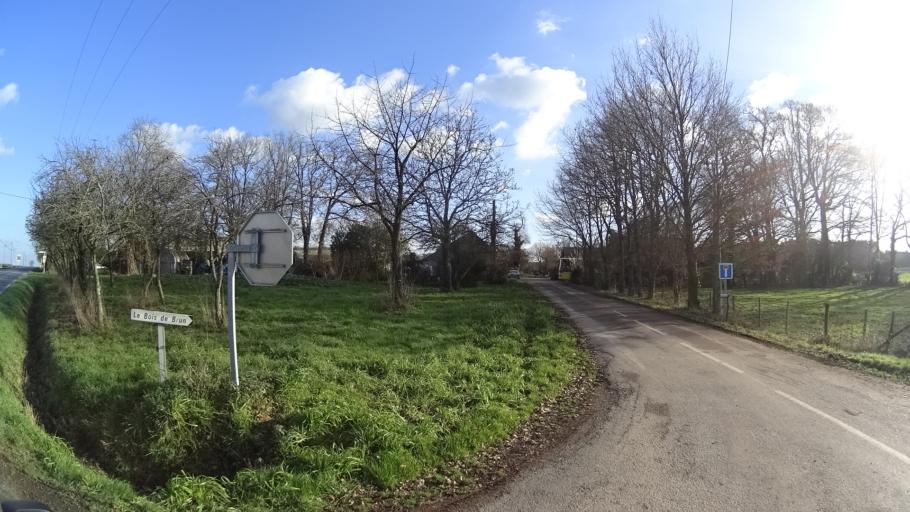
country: FR
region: Pays de la Loire
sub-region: Departement de la Loire-Atlantique
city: Guemene-Penfao
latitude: 47.6331
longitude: -1.8095
